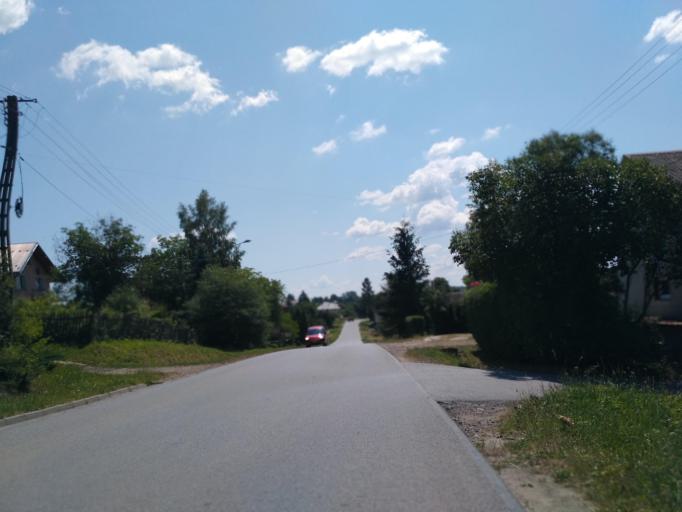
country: PL
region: Subcarpathian Voivodeship
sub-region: Powiat sanocki
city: Niebieszczany
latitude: 49.5161
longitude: 22.1386
